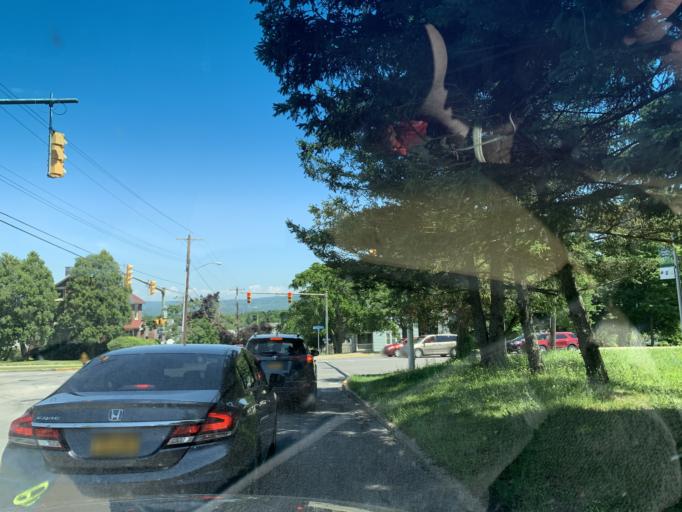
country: US
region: New York
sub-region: Oneida County
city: Utica
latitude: 43.0797
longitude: -75.2329
